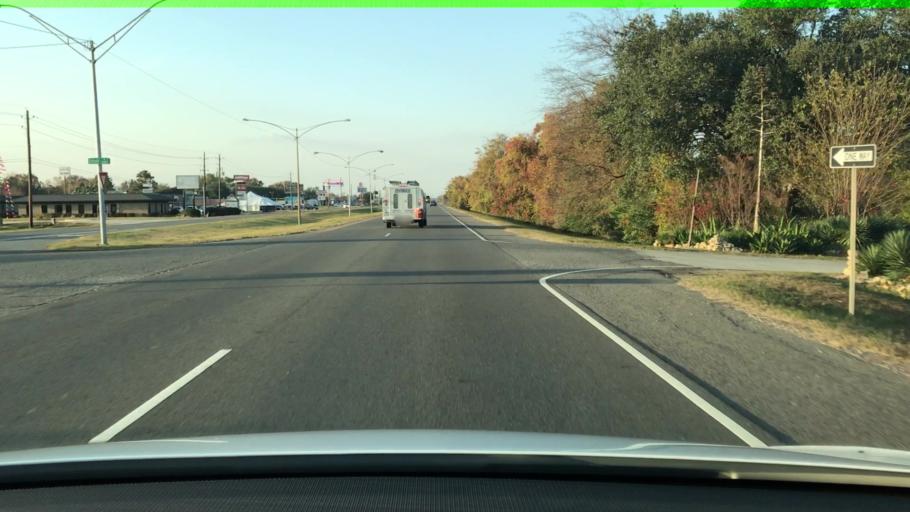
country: US
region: Louisiana
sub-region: Bossier Parish
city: Bossier City
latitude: 32.4207
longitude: -93.7053
